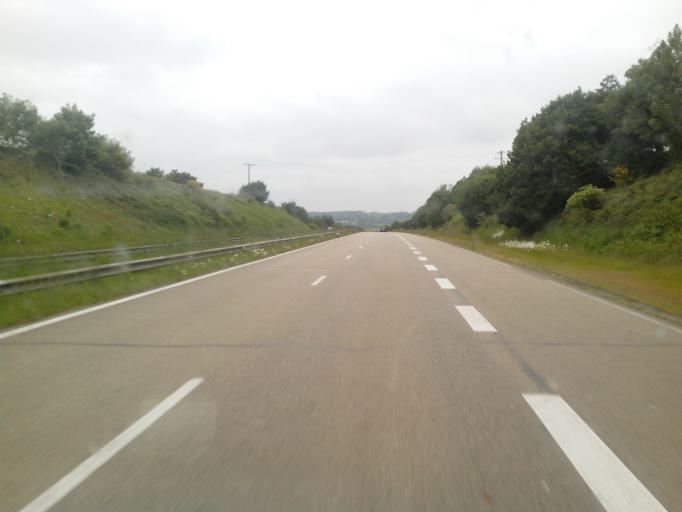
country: FR
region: Brittany
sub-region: Departement du Finistere
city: Guerlesquin
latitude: 48.5702
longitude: -3.6100
